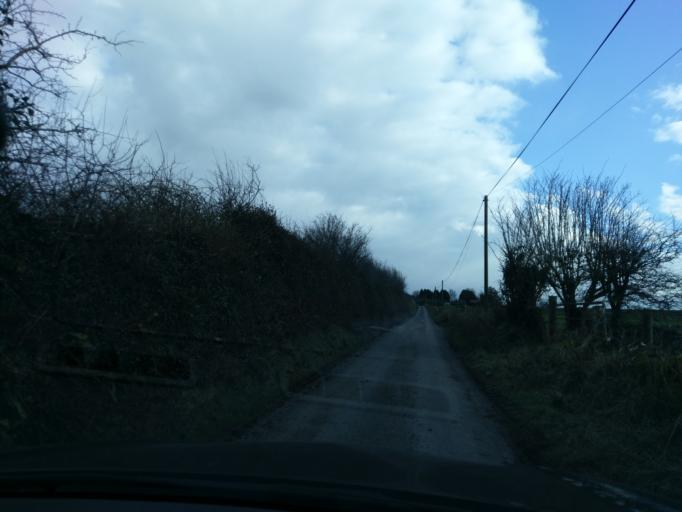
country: IE
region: Connaught
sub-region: County Galway
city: Athenry
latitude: 53.4540
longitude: -8.6694
